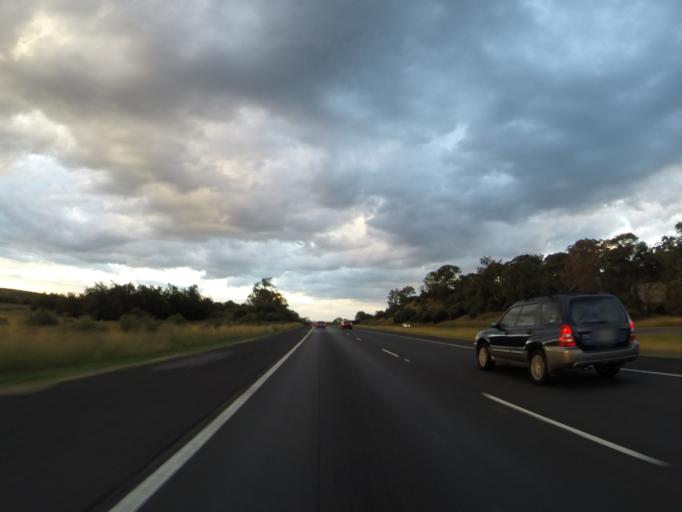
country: AU
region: New South Wales
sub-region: Campbelltown Municipality
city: Glen Alpine
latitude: -34.1110
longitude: 150.7605
